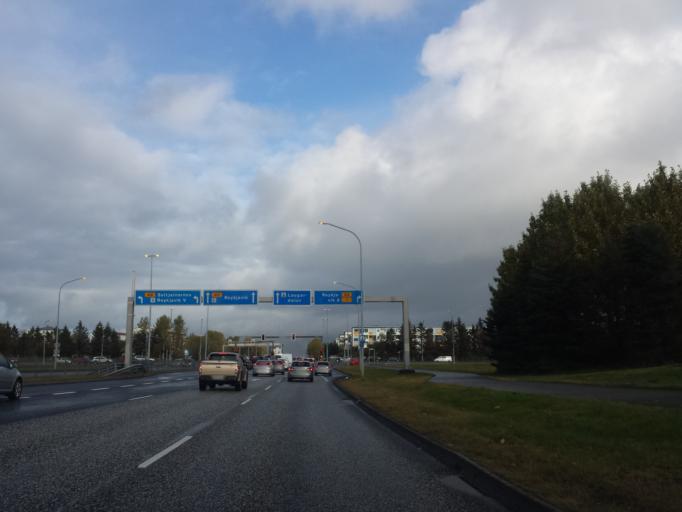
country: IS
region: Capital Region
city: Reykjavik
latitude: 64.1316
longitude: -21.8990
